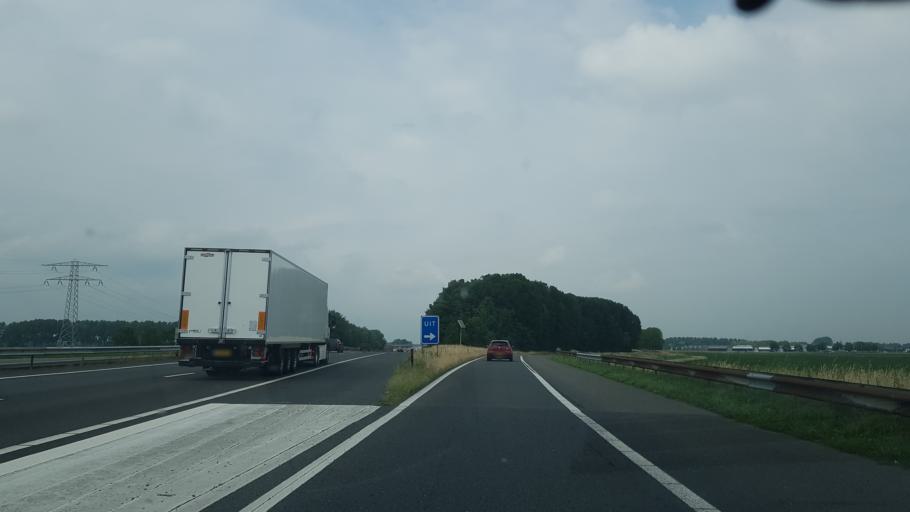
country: NL
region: North Brabant
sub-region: Gemeente Moerdijk
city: Willemstad
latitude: 51.7462
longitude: 4.4140
